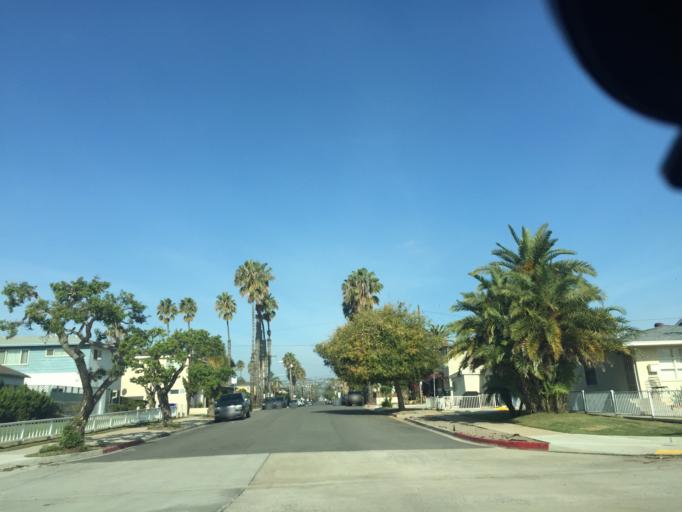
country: US
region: California
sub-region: San Diego County
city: La Jolla
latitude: 32.7942
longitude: -117.2469
